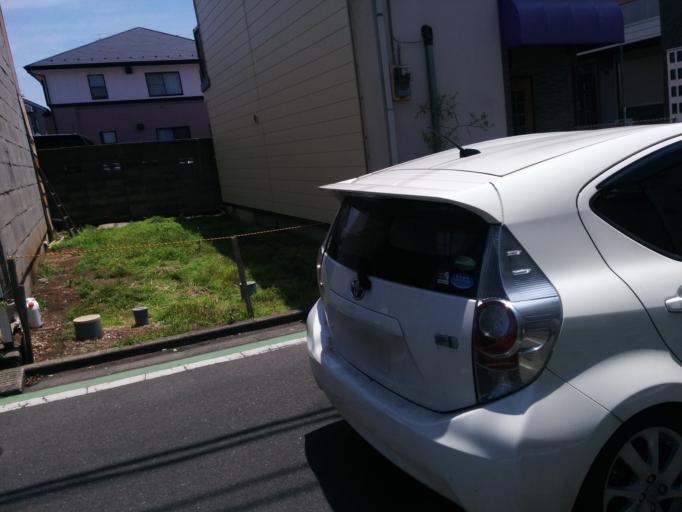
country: JP
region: Tokyo
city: Higashimurayama-shi
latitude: 35.7686
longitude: 139.4681
